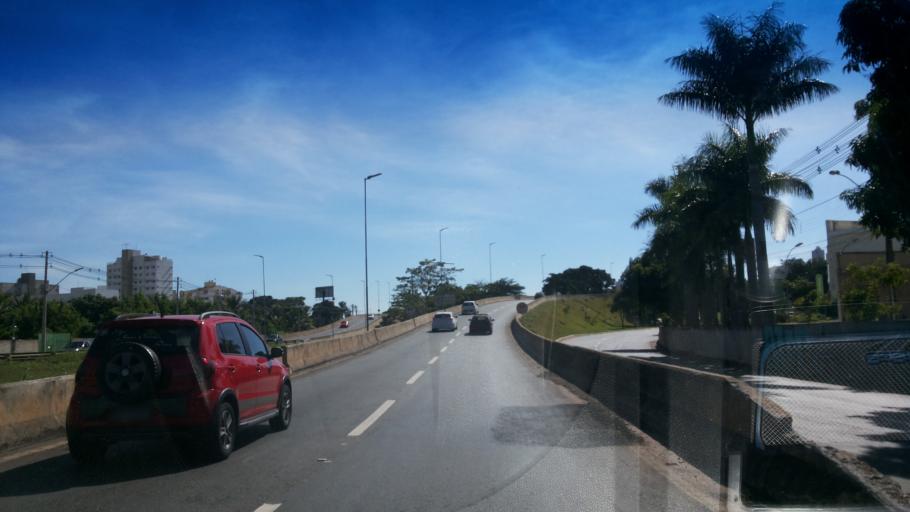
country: BR
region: Goias
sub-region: Goiania
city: Goiania
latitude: -16.6969
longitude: -49.2446
